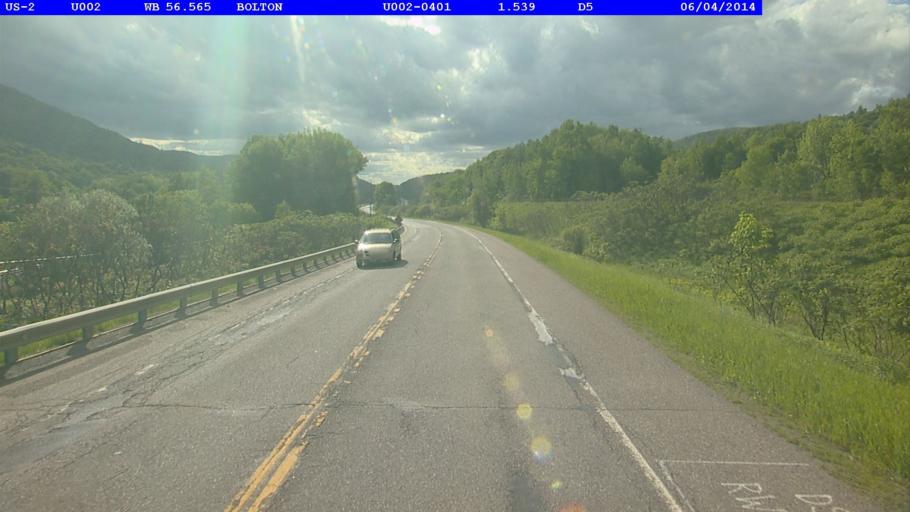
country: US
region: Vermont
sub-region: Washington County
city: Waterbury
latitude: 44.3777
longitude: -72.9035
